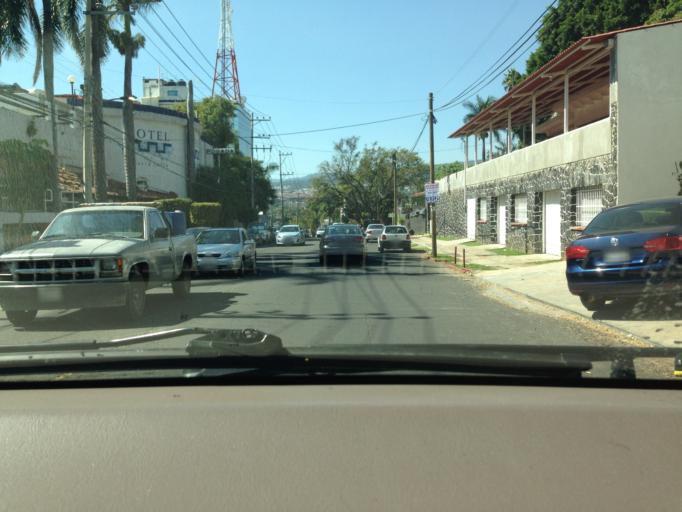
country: MX
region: Morelos
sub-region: Cuernavaca
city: Fraccionamiento Lomas de Ahuatlan
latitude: 18.9568
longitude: -99.2316
